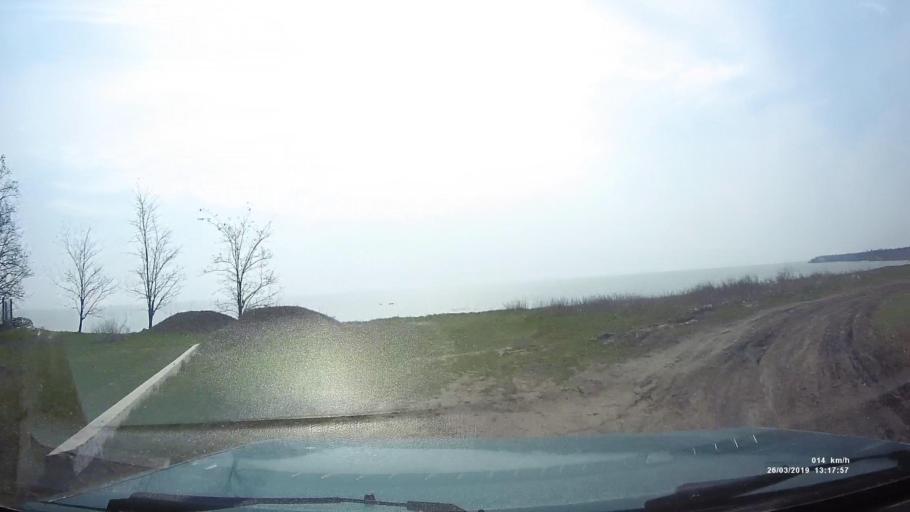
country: RU
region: Rostov
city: Novobessergenovka
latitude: 47.1700
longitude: 38.7675
